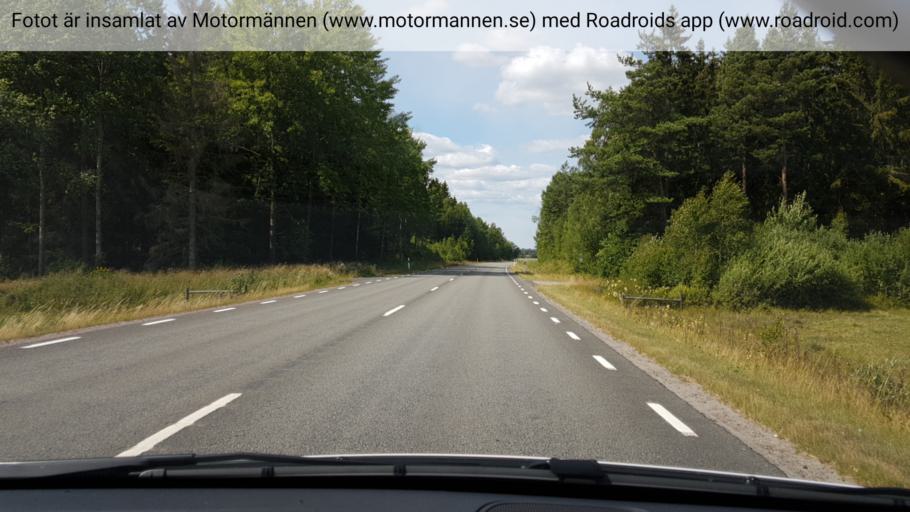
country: SE
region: Vaestra Goetaland
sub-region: Mariestads Kommun
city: Mariestad
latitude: 58.6183
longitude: 13.9580
